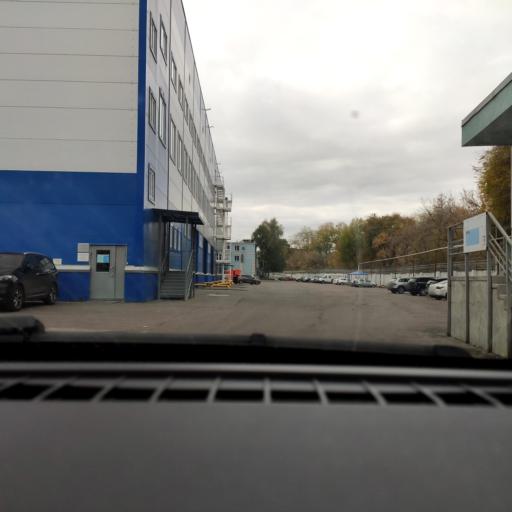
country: RU
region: Voronezj
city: Voronezh
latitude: 51.6559
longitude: 39.2816
